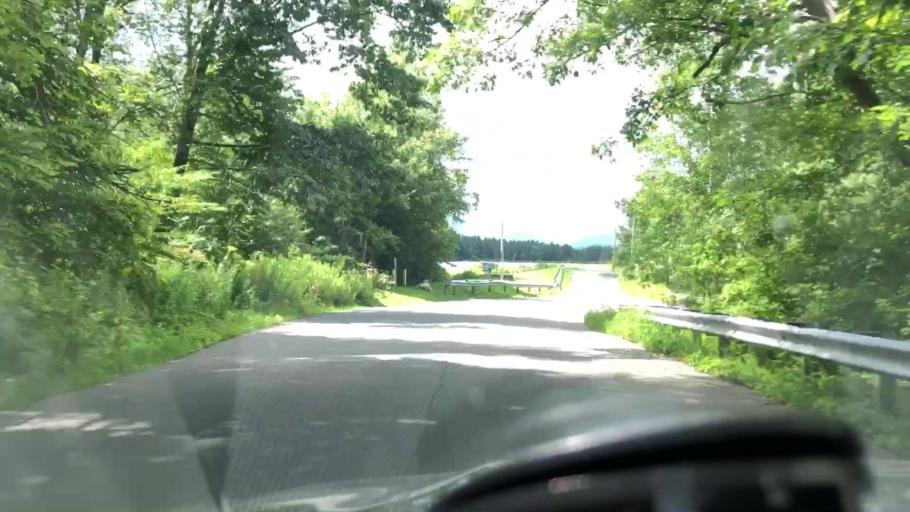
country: US
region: Massachusetts
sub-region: Berkshire County
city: North Adams
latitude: 42.6851
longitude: -73.1477
